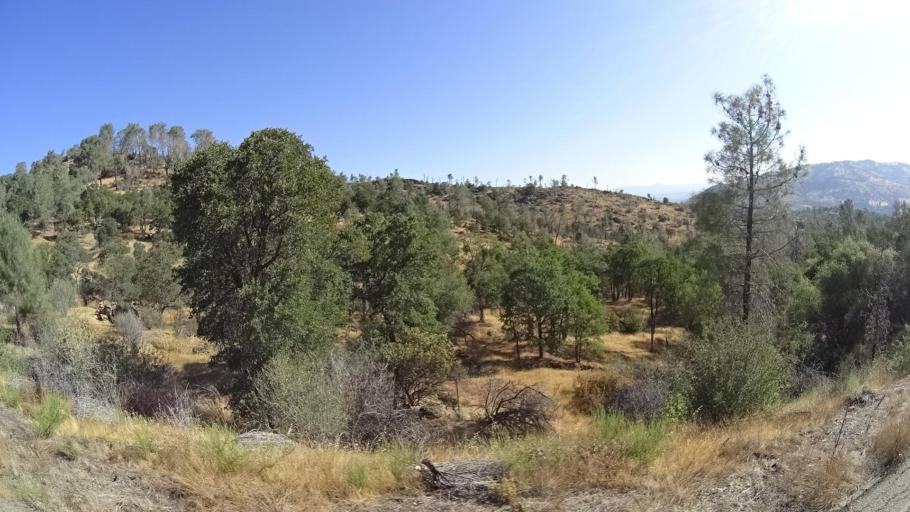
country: US
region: California
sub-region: Mariposa County
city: Mariposa
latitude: 37.5693
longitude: -120.1485
